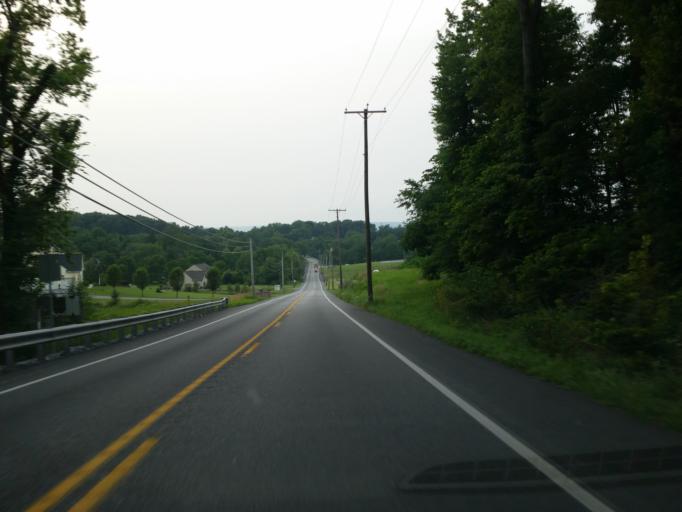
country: US
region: Pennsylvania
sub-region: Lebanon County
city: Annville
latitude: 40.3427
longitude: -76.5225
